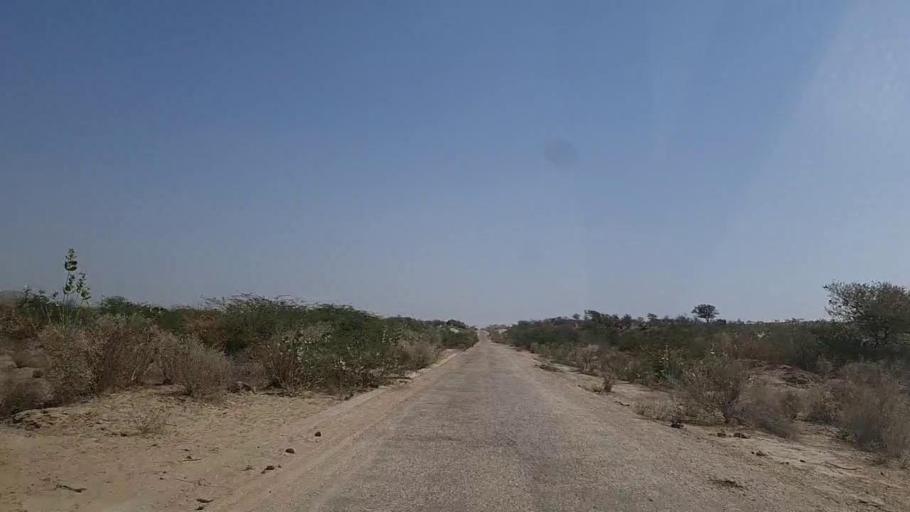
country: PK
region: Sindh
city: Diplo
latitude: 24.5137
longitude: 69.3973
